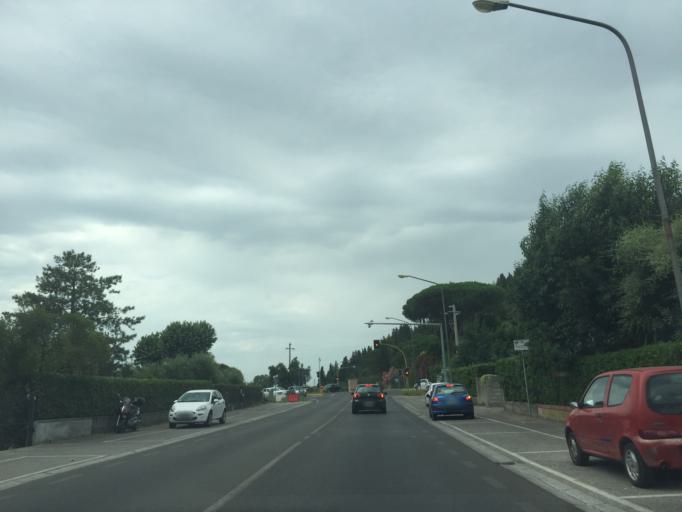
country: IT
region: Tuscany
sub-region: Province of Pisa
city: Gabella
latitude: 43.7241
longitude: 10.4951
